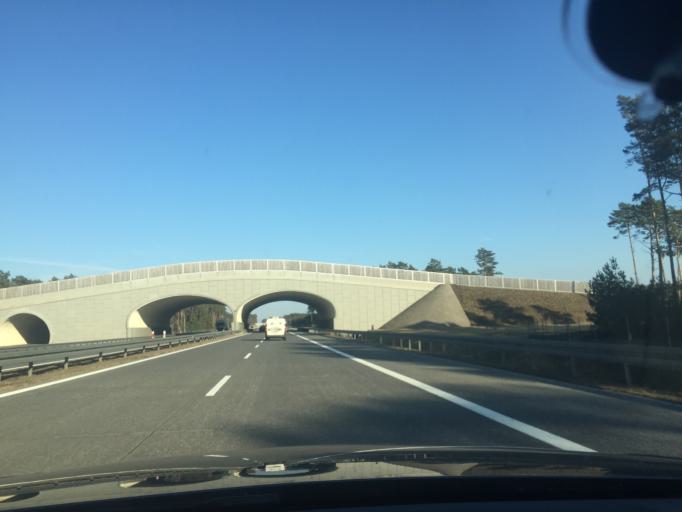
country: PL
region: Greater Poland Voivodeship
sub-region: Powiat nowotomyski
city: Nowy Tomysl
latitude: 52.3501
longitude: 16.0470
